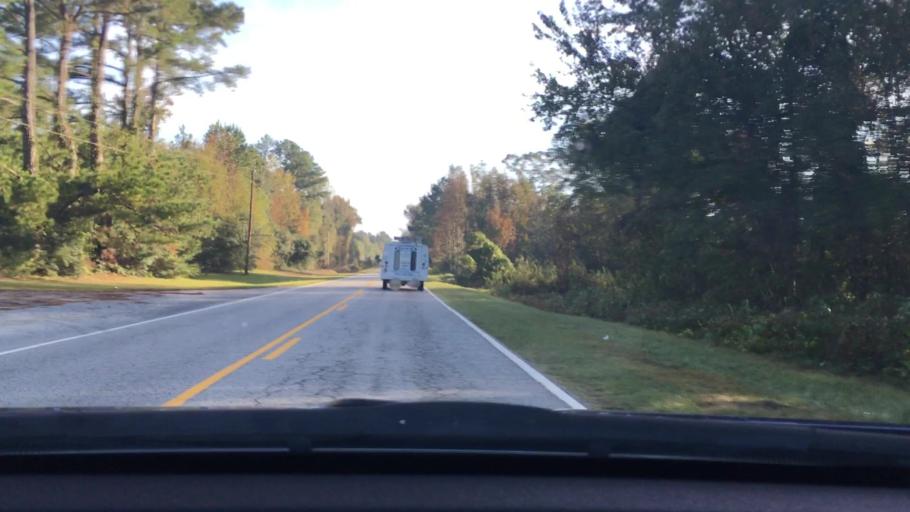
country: US
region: South Carolina
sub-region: Sumter County
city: East Sumter
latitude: 34.0415
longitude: -80.2612
